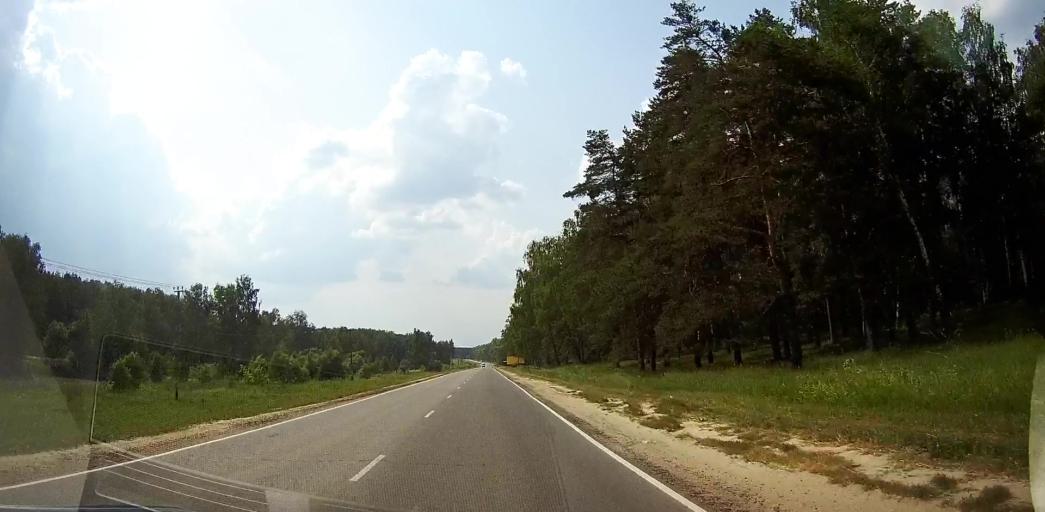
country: RU
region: Moskovskaya
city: Zhilevo
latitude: 55.0560
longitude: 37.9736
